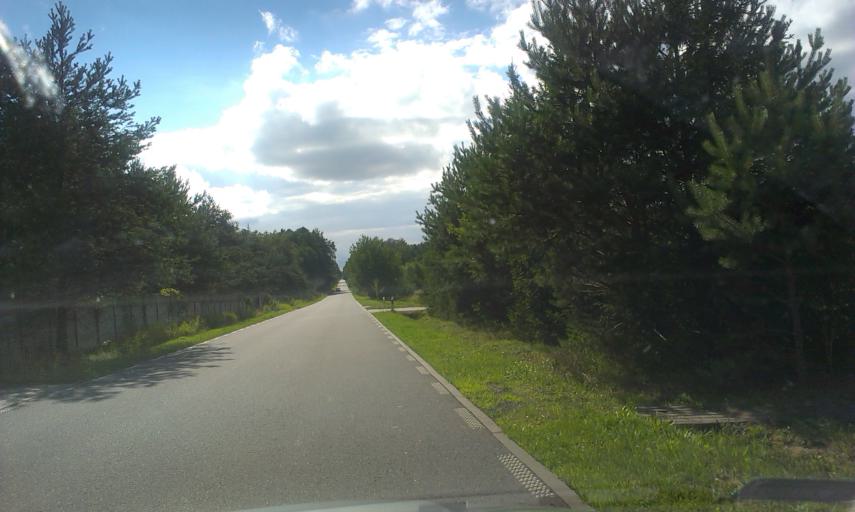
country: PL
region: Lodz Voivodeship
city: Zabia Wola
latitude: 51.9671
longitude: 20.6485
